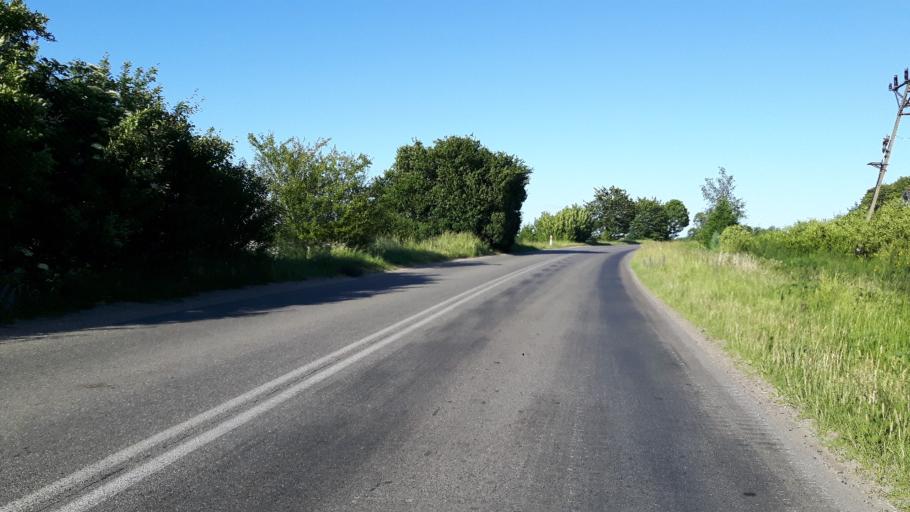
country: PL
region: Pomeranian Voivodeship
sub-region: Powiat wejherowski
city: Rumia
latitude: 54.6048
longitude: 18.4212
